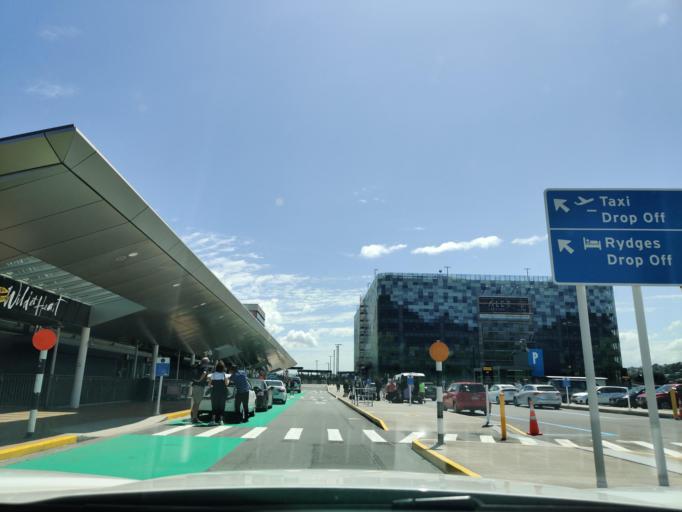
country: NZ
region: Wellington
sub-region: Wellington City
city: Wellington
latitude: -41.3295
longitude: 174.8122
